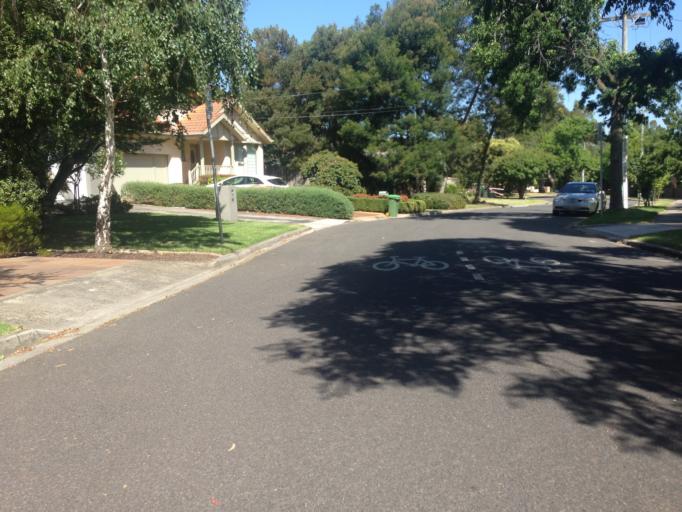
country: AU
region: Victoria
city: Ivanhoe East
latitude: -37.7730
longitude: 145.0475
